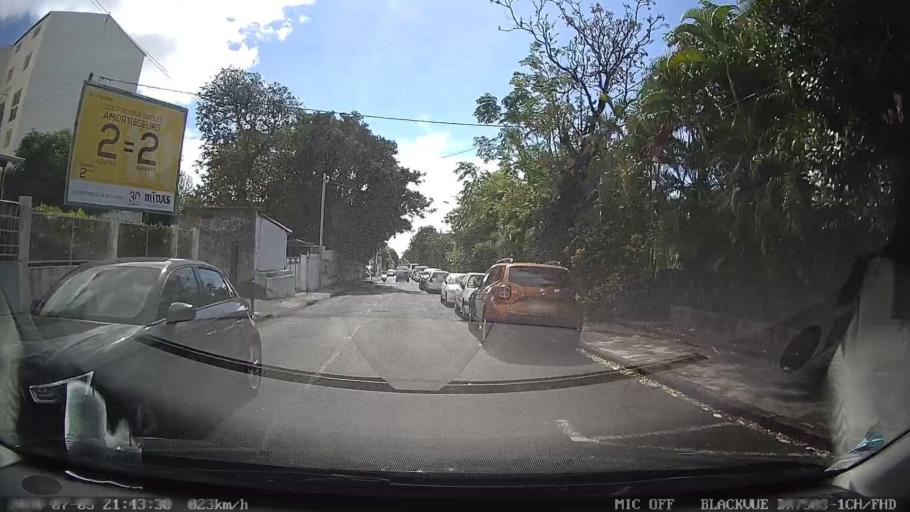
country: RE
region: Reunion
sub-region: Reunion
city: Saint-Denis
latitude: -20.8900
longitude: 55.4800
